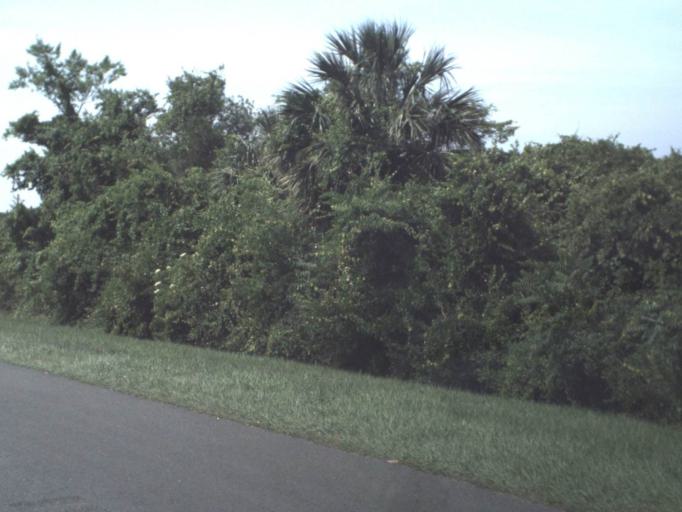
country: US
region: Florida
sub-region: Nassau County
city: Yulee
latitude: 30.5719
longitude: -81.6451
